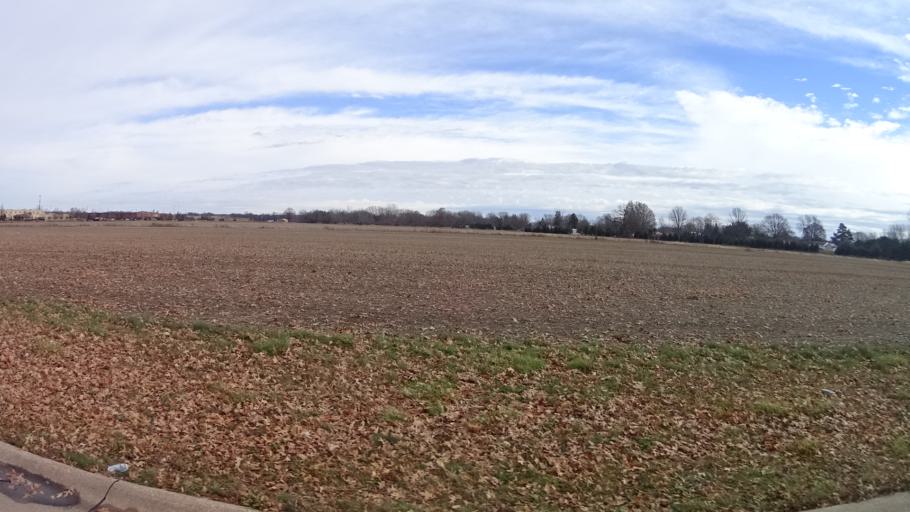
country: US
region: Ohio
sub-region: Lorain County
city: North Ridgeville
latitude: 41.3703
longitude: -82.0558
